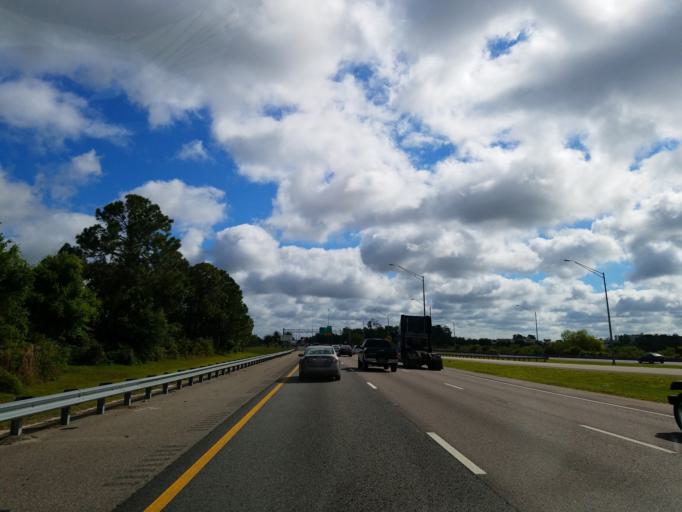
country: US
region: Florida
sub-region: Osceola County
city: Celebration
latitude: 28.3165
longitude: -81.5602
